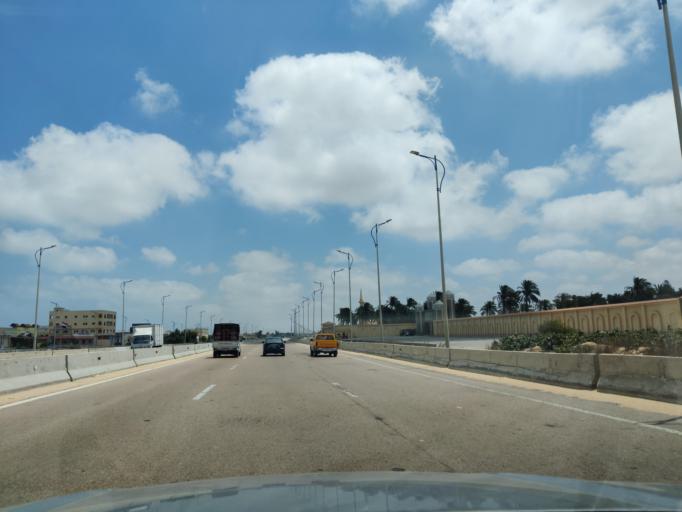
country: EG
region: Alexandria
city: Alexandria
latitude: 30.9838
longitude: 29.5831
